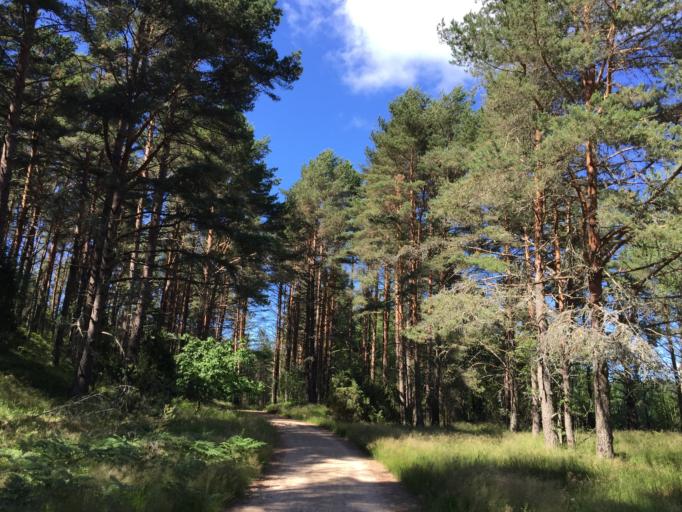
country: LV
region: Ventspils
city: Ventspils
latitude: 57.4509
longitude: 21.6299
